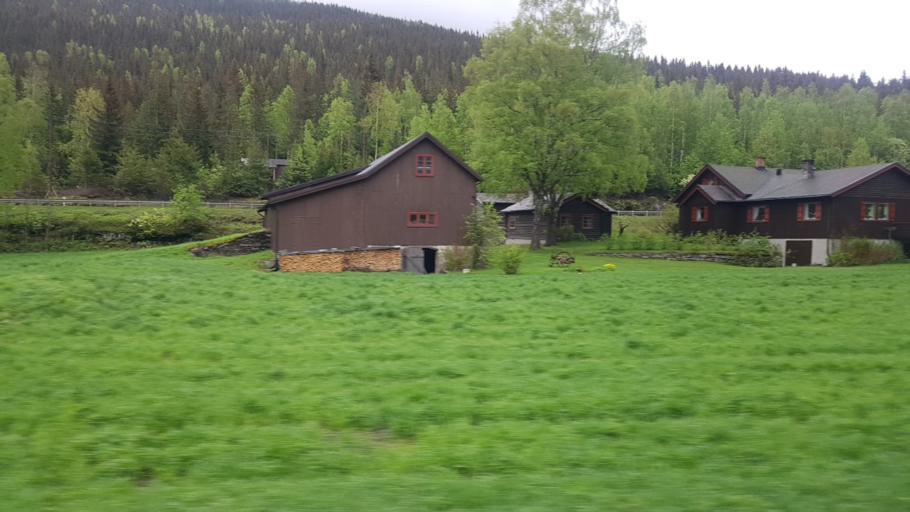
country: NO
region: Oppland
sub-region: Nord-Fron
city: Vinstra
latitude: 61.6198
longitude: 9.7121
